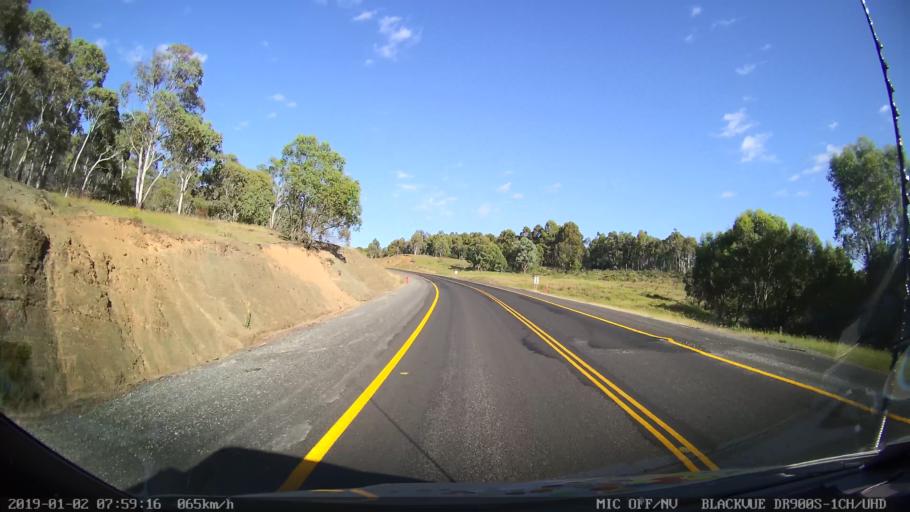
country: AU
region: New South Wales
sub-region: Tumut Shire
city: Tumut
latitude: -35.6460
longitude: 148.4604
